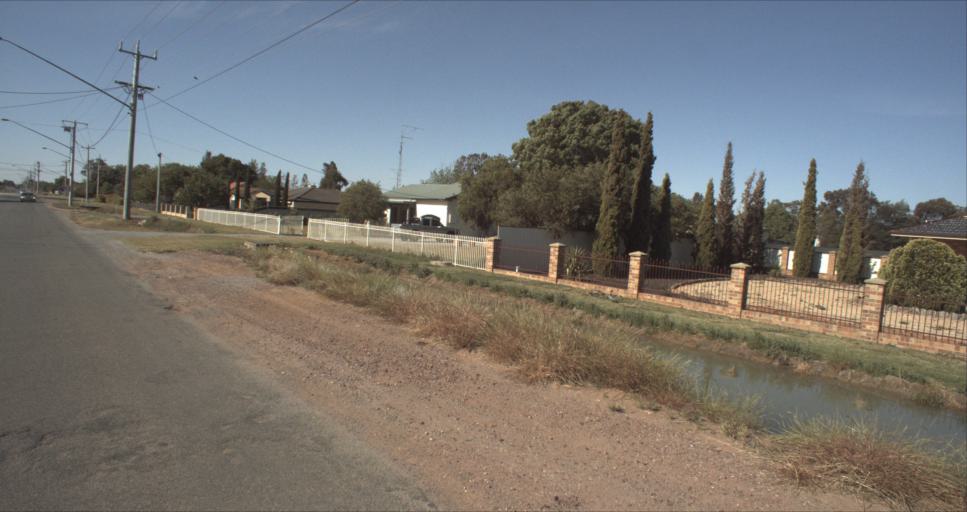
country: AU
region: New South Wales
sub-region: Leeton
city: Leeton
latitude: -34.5584
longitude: 146.4158
